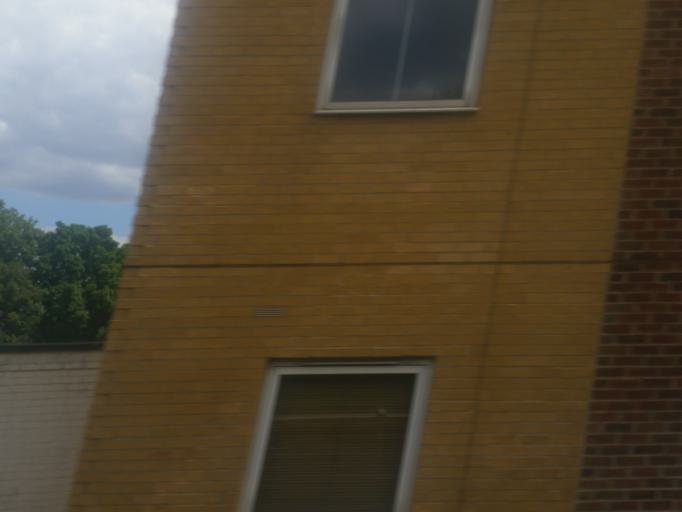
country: GB
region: England
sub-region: Greater London
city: Camberwell
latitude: 51.4840
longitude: -0.0956
